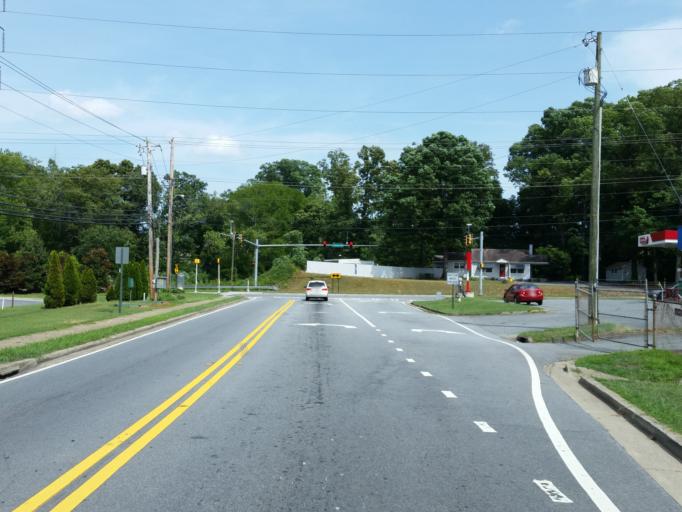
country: US
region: Georgia
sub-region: Cherokee County
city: Woodstock
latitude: 34.0495
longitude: -84.5281
